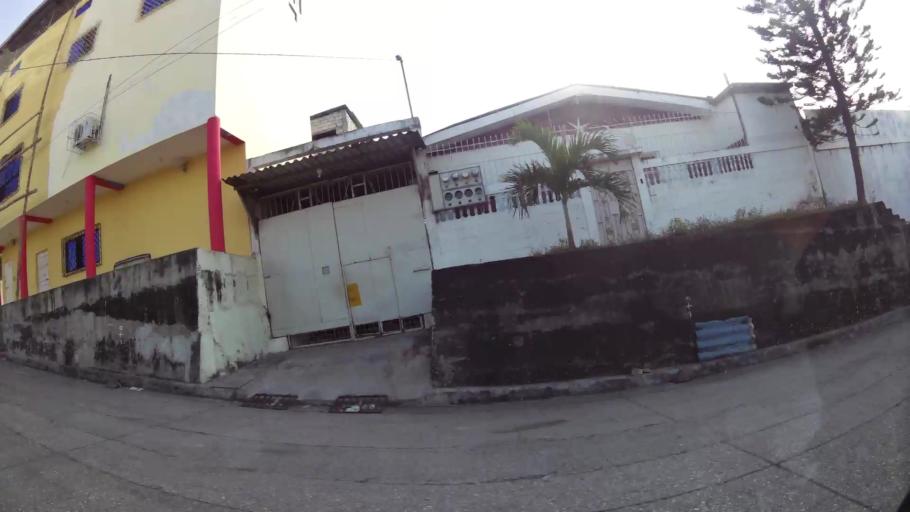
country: EC
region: Guayas
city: Guayaquil
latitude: -2.1426
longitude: -79.9302
